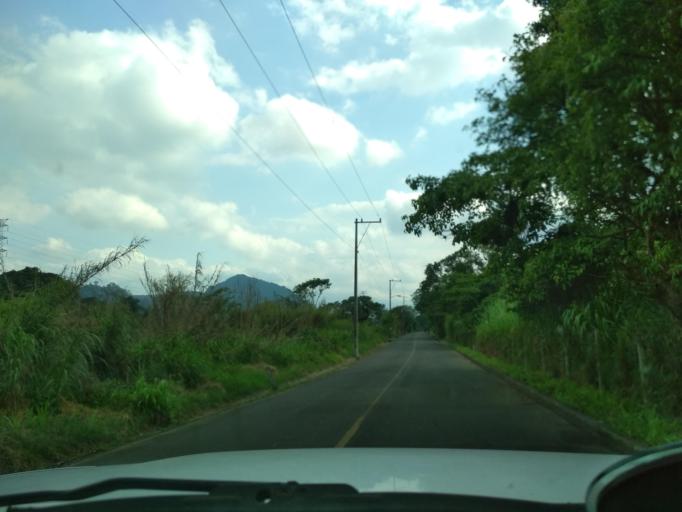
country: MX
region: Veracruz
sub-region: Ixtaczoquitlan
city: Buenavista
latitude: 18.9107
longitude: -97.0276
